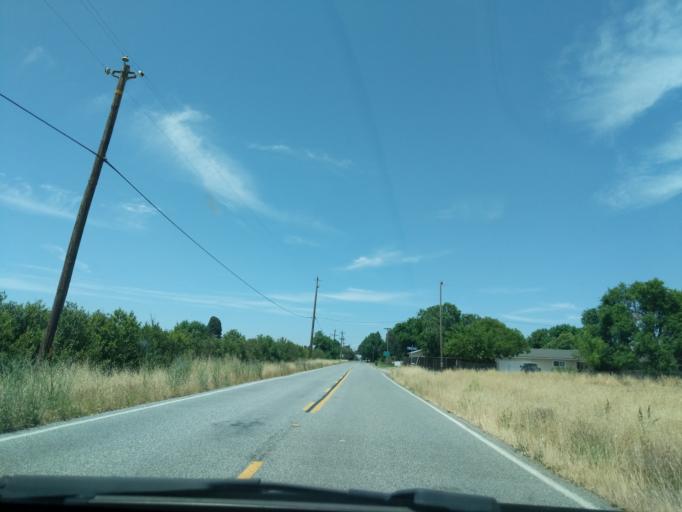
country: US
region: California
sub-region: Santa Clara County
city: San Martin
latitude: 37.0618
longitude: -121.5696
